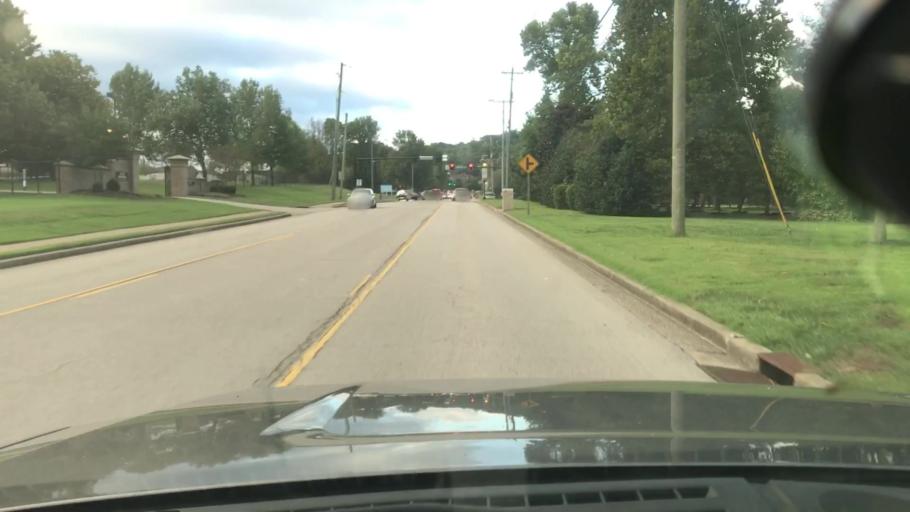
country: US
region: Tennessee
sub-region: Williamson County
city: Brentwood
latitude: 36.0203
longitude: -86.8207
